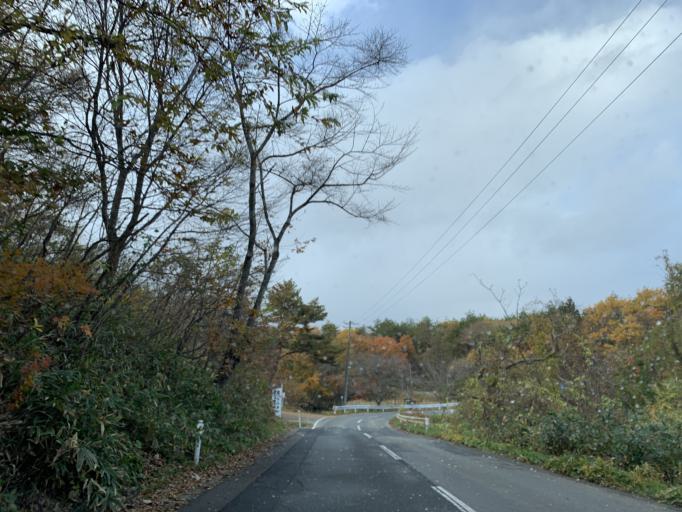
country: JP
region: Iwate
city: Mizusawa
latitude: 39.0447
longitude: 141.0761
